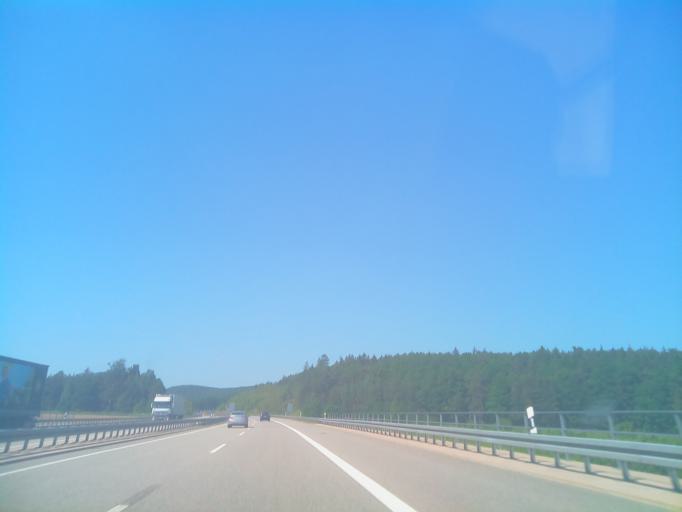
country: DE
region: Thuringia
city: Wolfershausen
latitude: 50.4624
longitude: 10.4535
